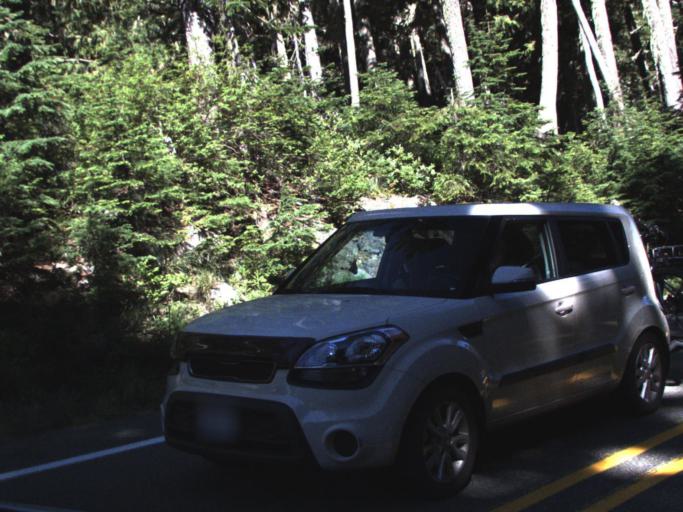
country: US
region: Washington
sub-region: King County
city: Enumclaw
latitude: 46.8748
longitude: -121.5407
